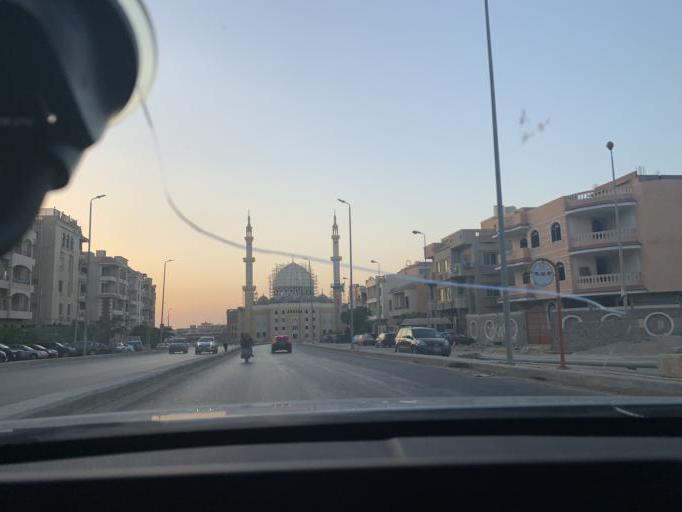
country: EG
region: Muhafazat al Qahirah
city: Cairo
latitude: 30.0039
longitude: 31.4586
